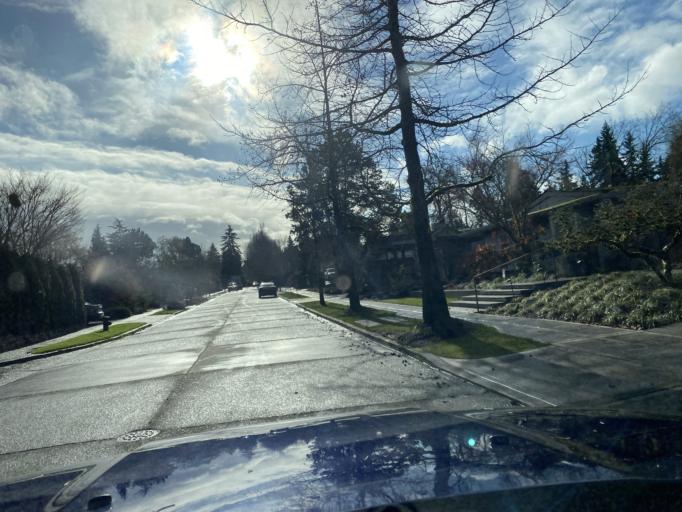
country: US
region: Washington
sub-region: King County
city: Seattle
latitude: 47.6397
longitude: -122.2849
